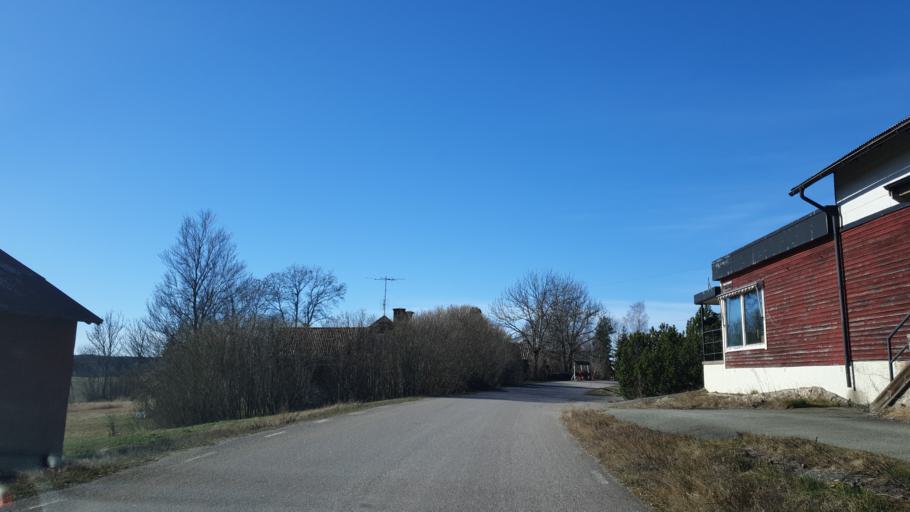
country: SE
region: Uppsala
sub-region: Enkopings Kommun
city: Dalby
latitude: 59.5211
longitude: 17.2768
